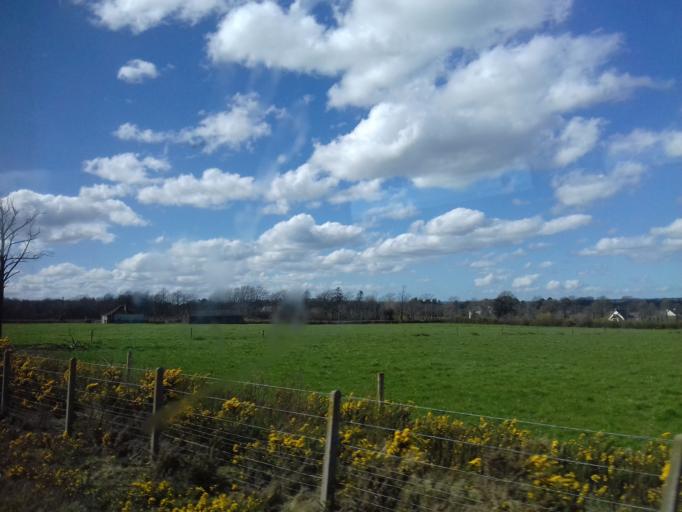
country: IE
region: Munster
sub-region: County Cork
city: Kanturk
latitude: 52.1290
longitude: -8.8437
